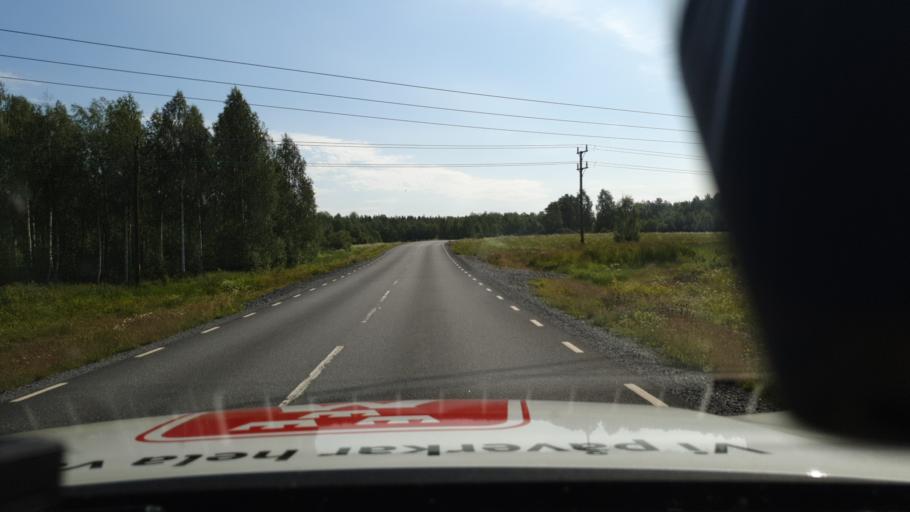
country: SE
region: Norrbotten
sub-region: Bodens Kommun
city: Saevast
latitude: 65.8444
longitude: 21.7871
